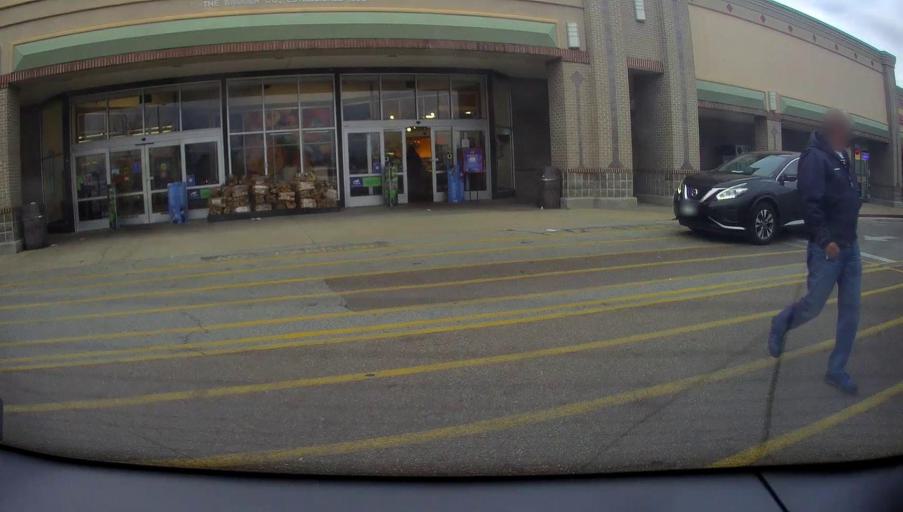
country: US
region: Tennessee
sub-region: Shelby County
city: Germantown
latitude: 35.0497
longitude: -89.7978
